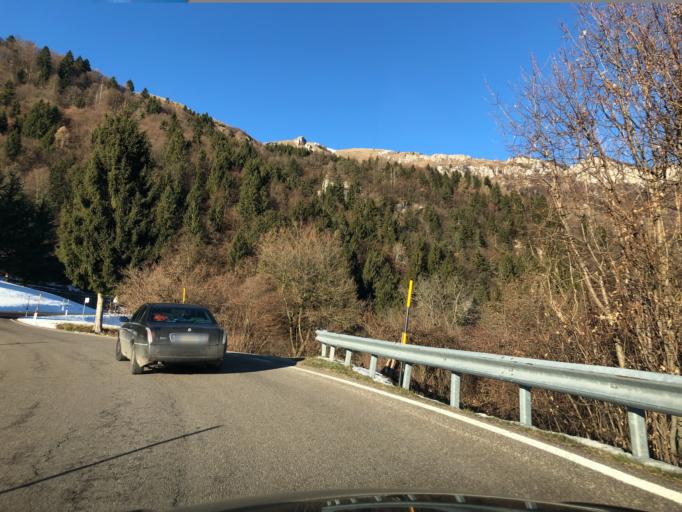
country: IT
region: Trentino-Alto Adige
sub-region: Provincia di Trento
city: Brentonico
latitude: 45.8093
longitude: 10.9353
